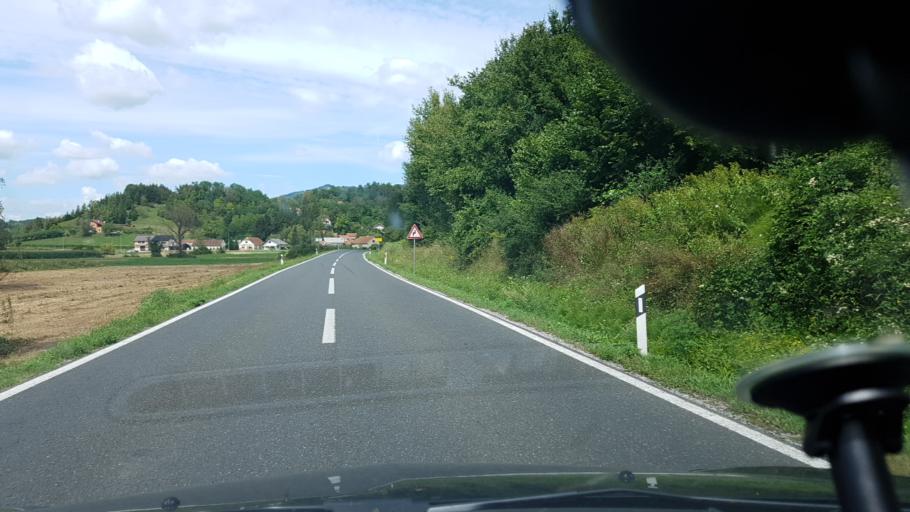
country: HR
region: Varazdinska
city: Lepoglava
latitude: 46.2259
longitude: 15.9933
